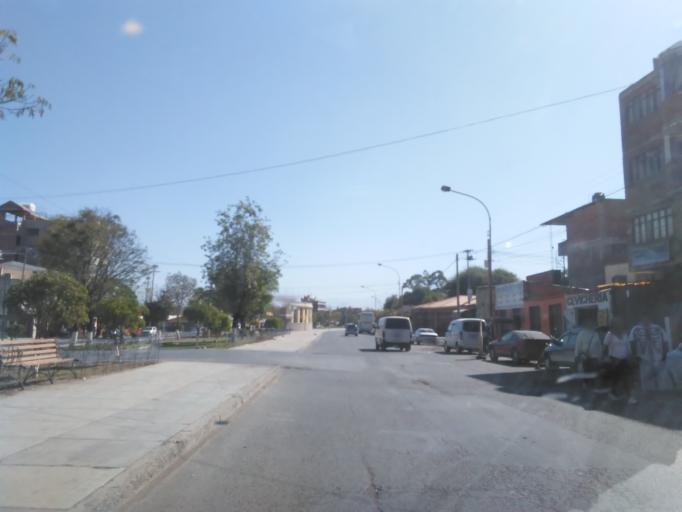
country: BO
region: Cochabamba
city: Cochabamba
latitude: -17.4132
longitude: -66.1573
